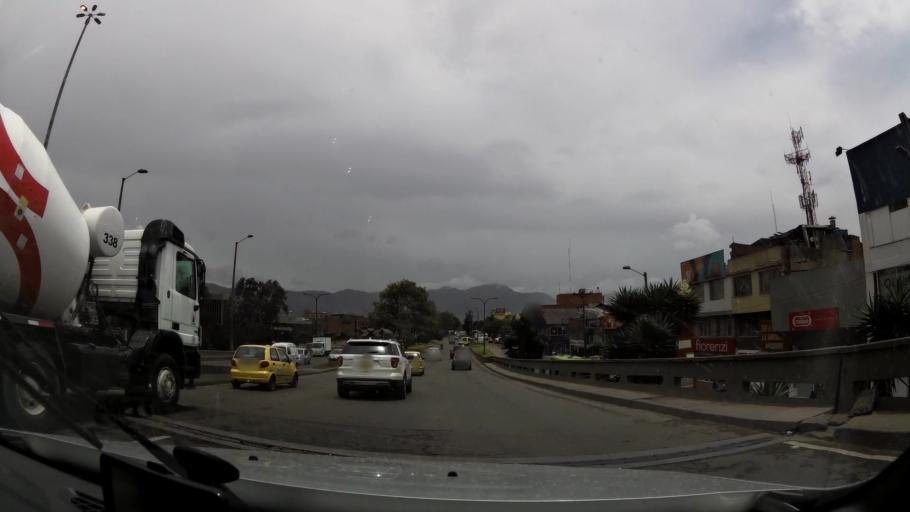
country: CO
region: Bogota D.C.
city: Bogota
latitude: 4.6366
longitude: -74.1178
